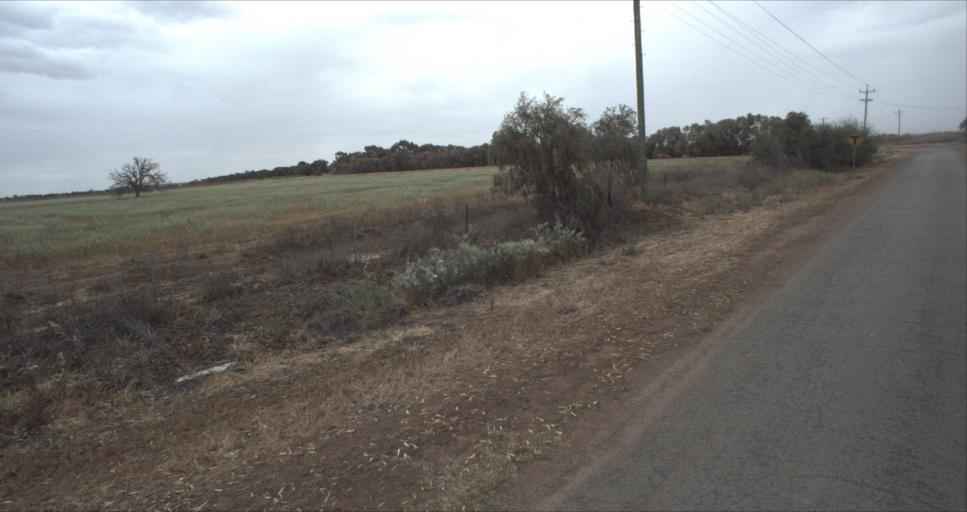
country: AU
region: New South Wales
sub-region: Leeton
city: Leeton
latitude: -34.4050
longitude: 146.3414
